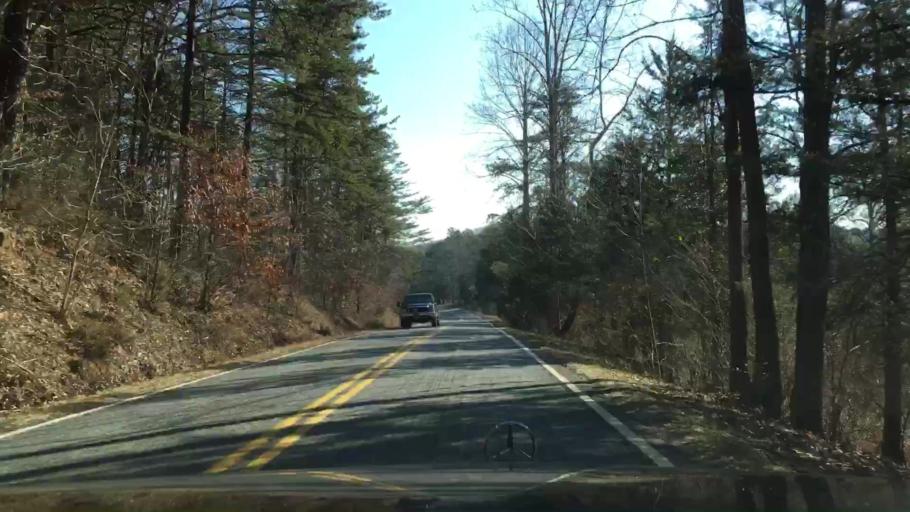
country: US
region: Virginia
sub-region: Campbell County
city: Altavista
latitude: 37.1538
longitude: -79.3600
